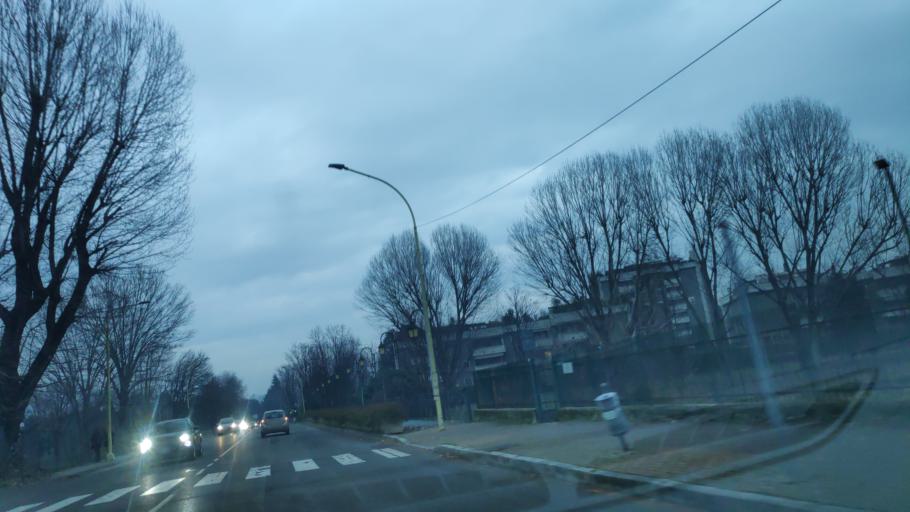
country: IT
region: Lombardy
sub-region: Citta metropolitana di Milano
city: Romano Banco
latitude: 45.4226
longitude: 9.1218
